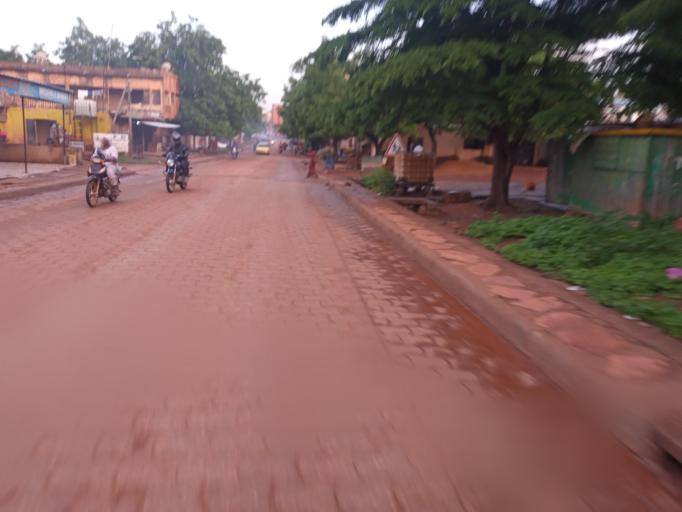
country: ML
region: Bamako
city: Bamako
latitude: 12.6428
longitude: -8.0311
